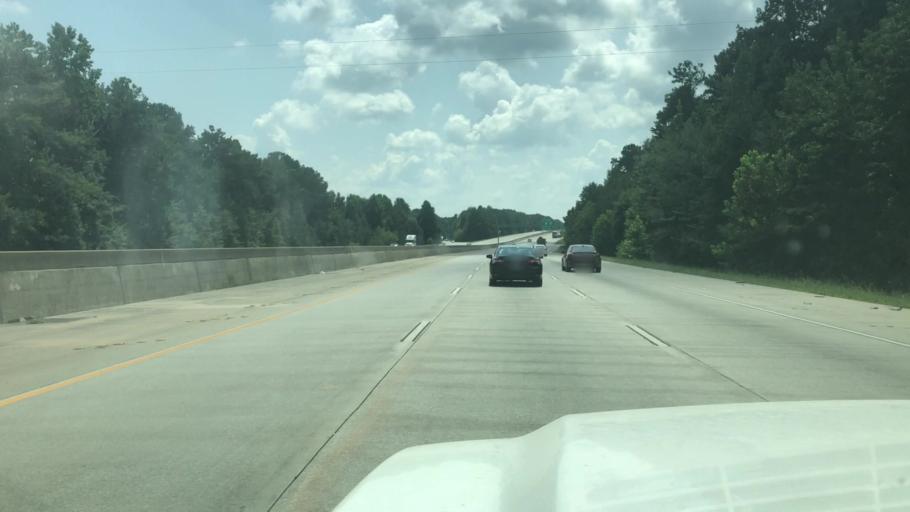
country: US
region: Georgia
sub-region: Coweta County
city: East Newnan
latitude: 33.3298
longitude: -84.7727
